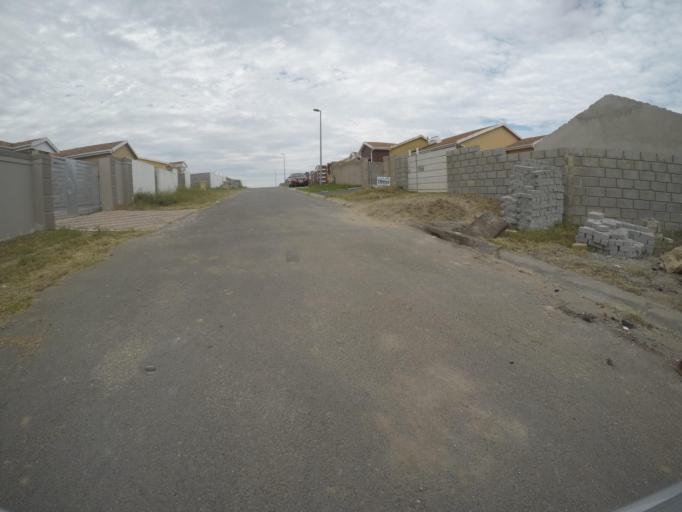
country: ZA
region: Eastern Cape
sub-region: Buffalo City Metropolitan Municipality
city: East London
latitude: -32.9929
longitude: 27.8427
